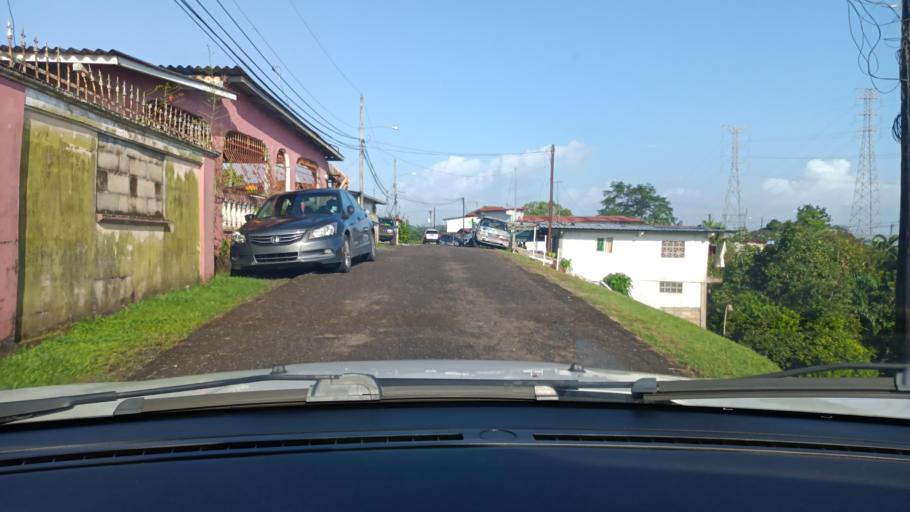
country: PA
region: Colon
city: Sabanitas
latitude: 9.3450
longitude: -79.8022
